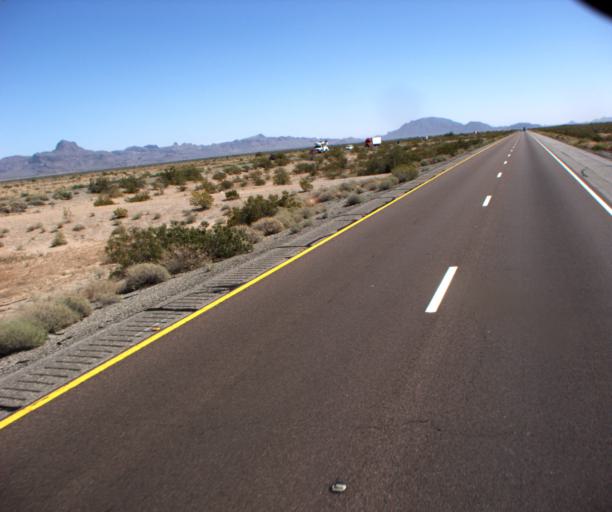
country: US
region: Arizona
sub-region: La Paz County
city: Salome
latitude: 33.5545
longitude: -113.2596
